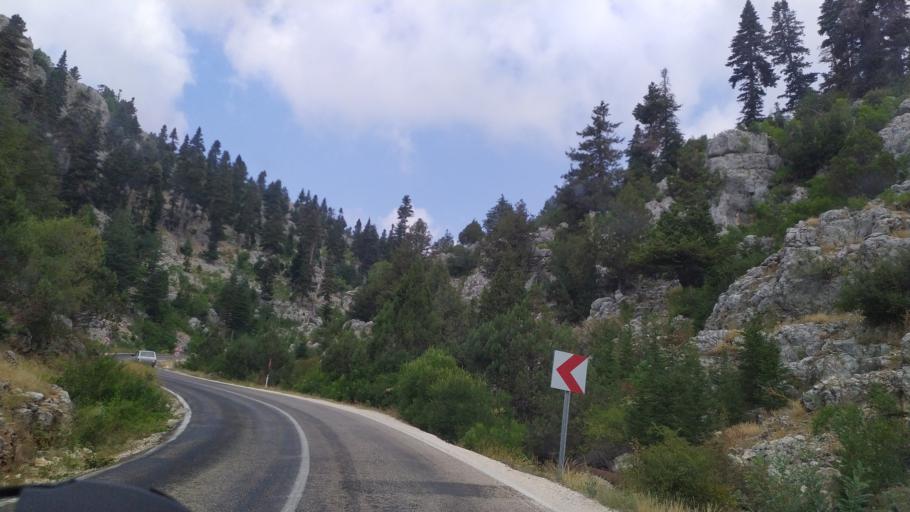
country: TR
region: Mersin
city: Kirobasi
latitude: 36.6066
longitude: 33.8853
